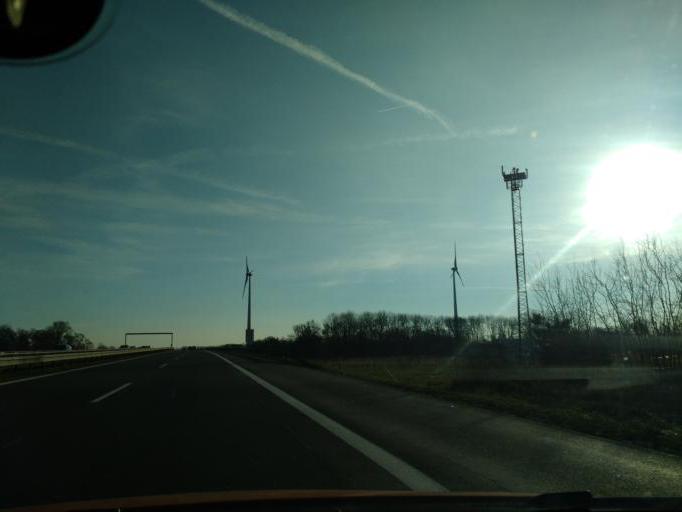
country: DE
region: Berlin
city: Buchholz
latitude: 52.6373
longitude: 13.4374
